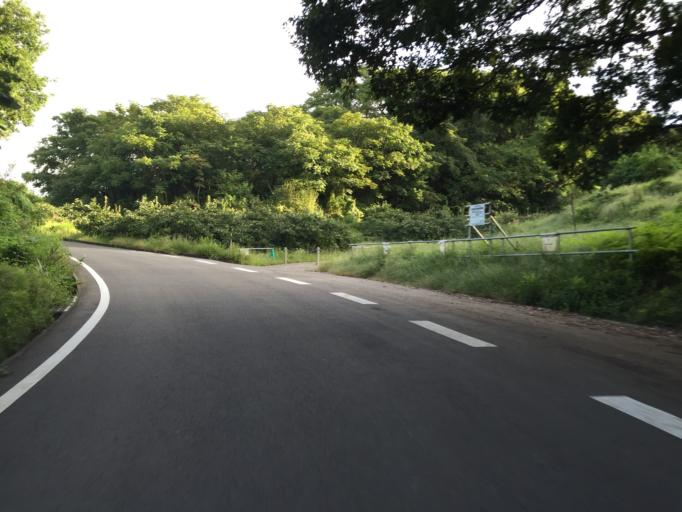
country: JP
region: Fukushima
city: Hobaramachi
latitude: 37.8046
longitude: 140.5406
